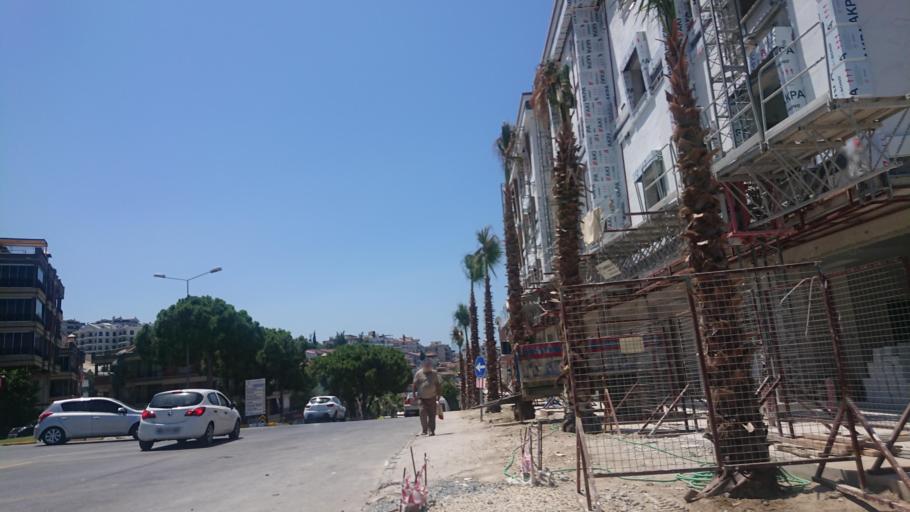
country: TR
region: Aydin
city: Kusadasi
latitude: 37.8657
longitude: 27.2680
